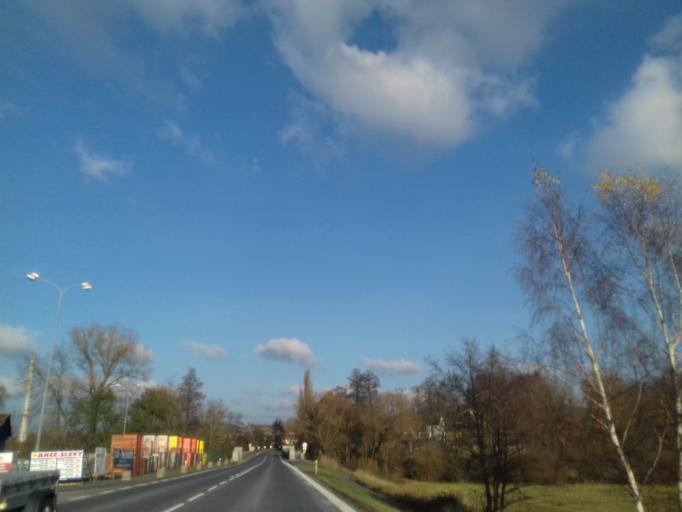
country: CZ
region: Plzensky
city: Holysov
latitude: 49.5914
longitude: 13.0918
